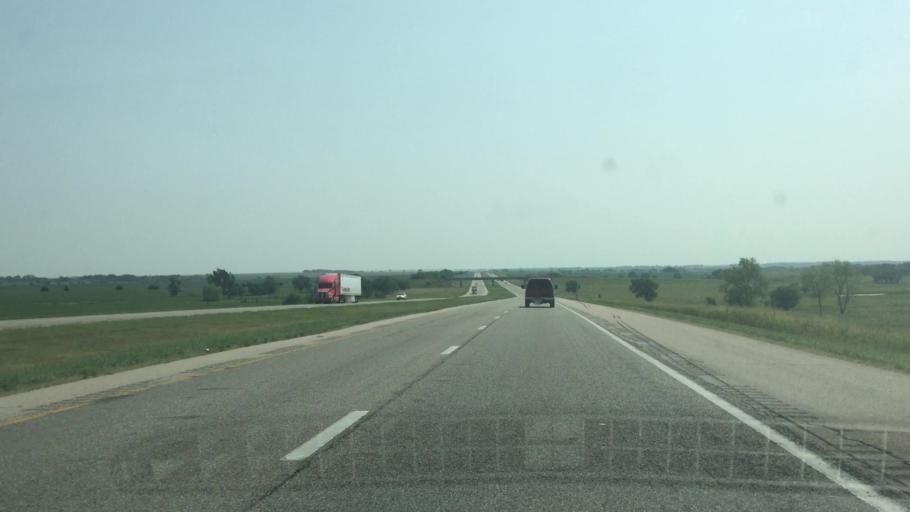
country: US
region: Kansas
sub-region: Osage County
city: Osage City
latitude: 38.4257
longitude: -95.8303
